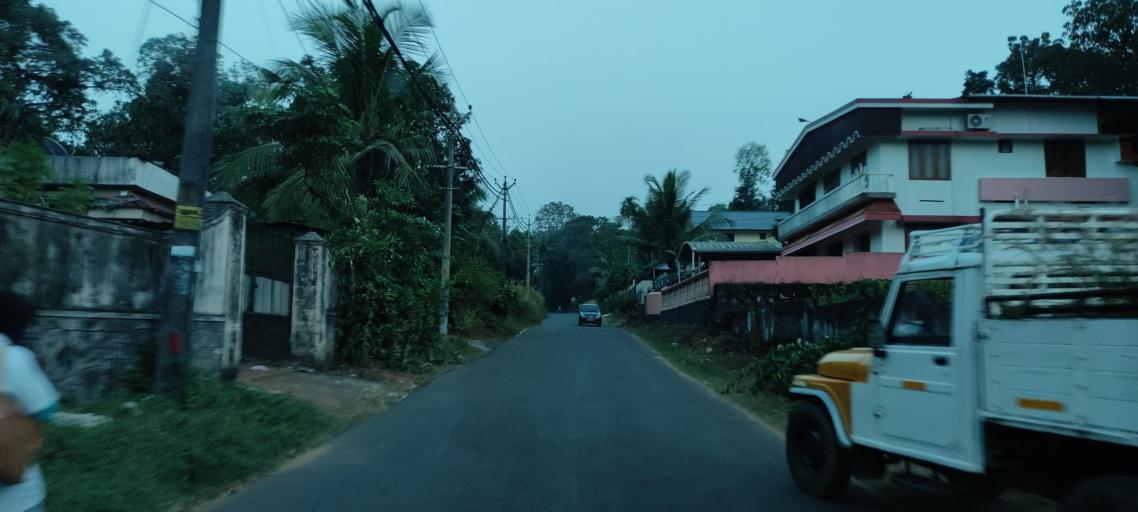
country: IN
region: Kerala
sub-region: Pattanamtitta
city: Adur
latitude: 9.1608
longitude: 76.7459
